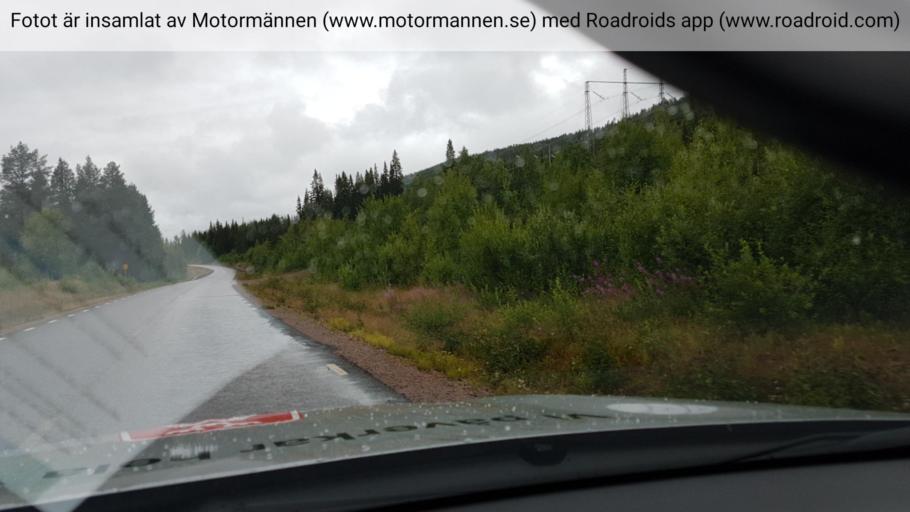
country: SE
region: Norrbotten
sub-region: Gallivare Kommun
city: Gaellivare
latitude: 66.6330
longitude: 20.4064
